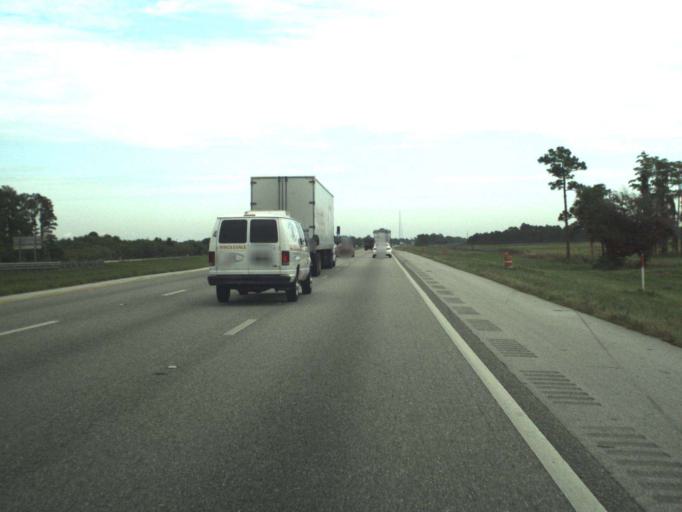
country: US
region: Florida
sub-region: Martin County
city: Port Salerno
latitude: 27.0595
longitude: -80.2387
